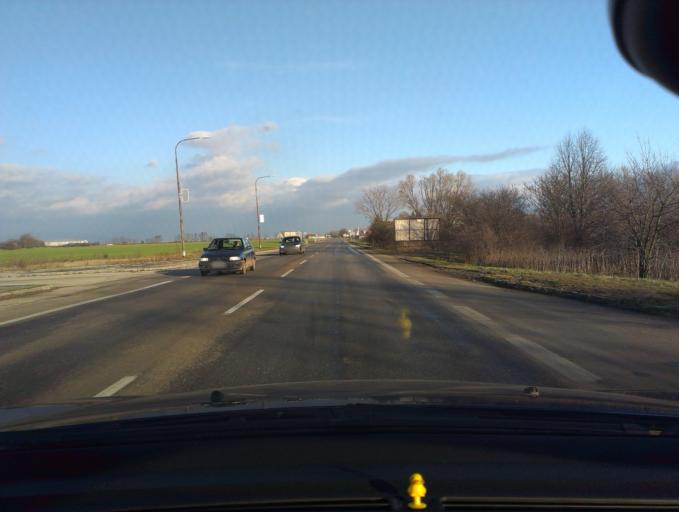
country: SK
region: Trnavsky
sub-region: Okres Trnava
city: Piestany
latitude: 48.6113
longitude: 17.8341
